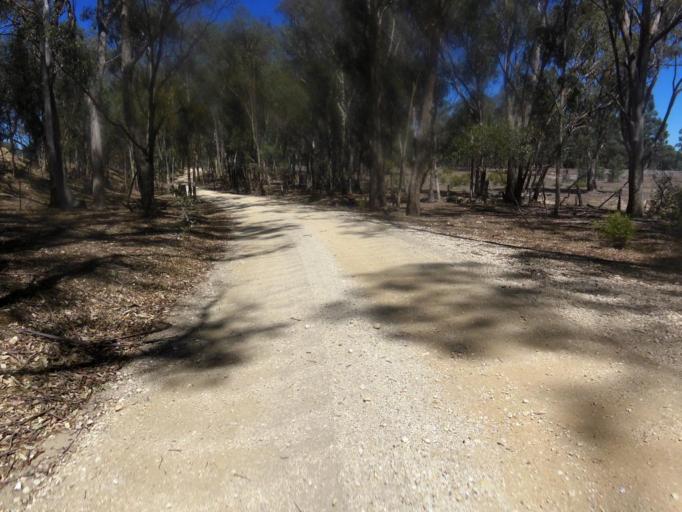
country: AU
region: Victoria
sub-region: Mount Alexander
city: Castlemaine
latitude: -37.0489
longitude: 144.1819
